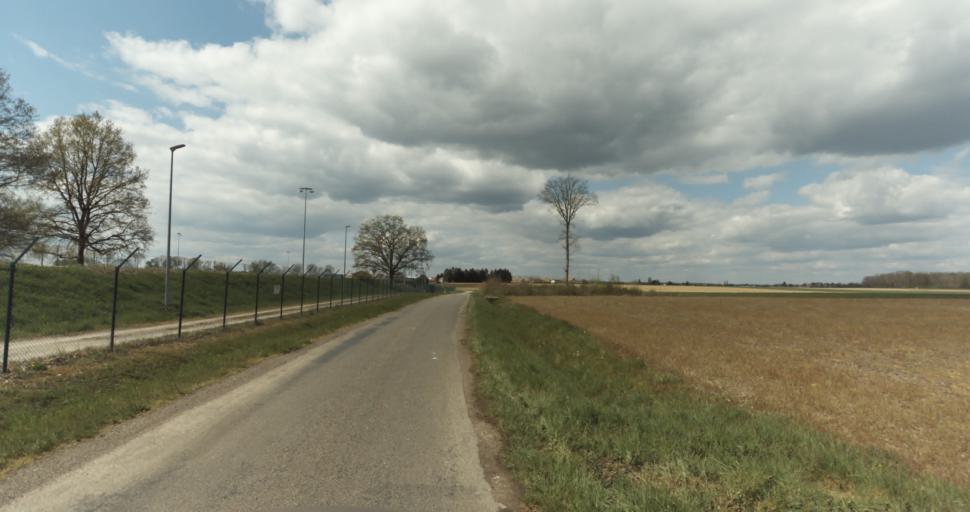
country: FR
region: Bourgogne
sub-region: Departement de la Cote-d'Or
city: Auxonne
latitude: 47.1759
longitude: 5.4110
